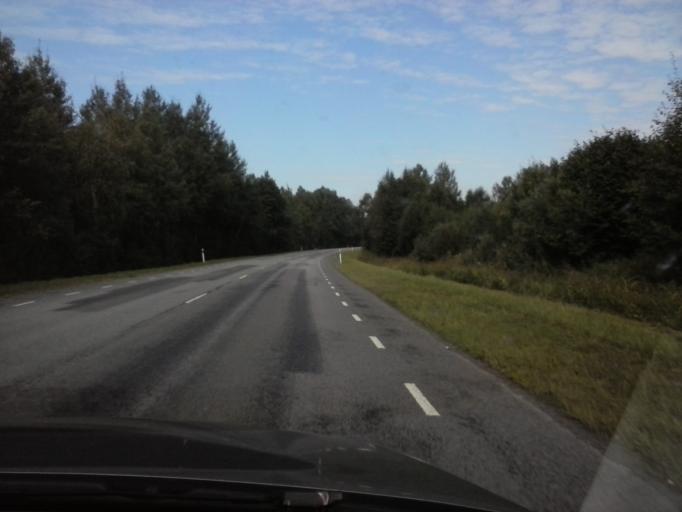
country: EE
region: Laeaene
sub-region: Ridala Parish
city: Uuemoisa
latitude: 58.8330
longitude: 23.6721
